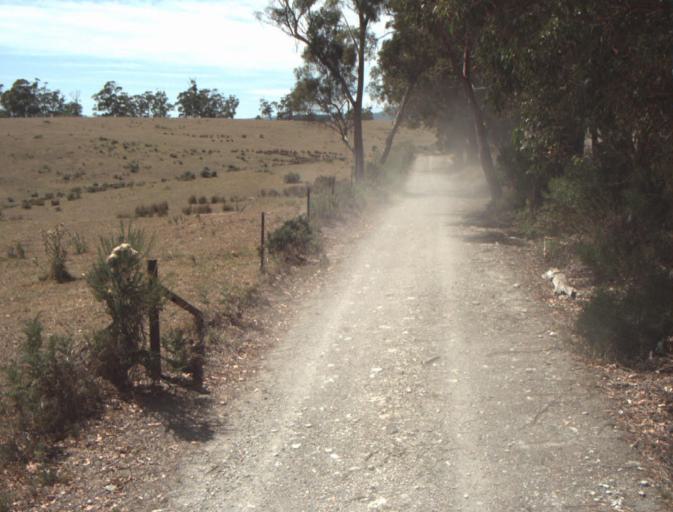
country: AU
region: Tasmania
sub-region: Launceston
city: Mayfield
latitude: -41.2474
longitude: 147.1683
